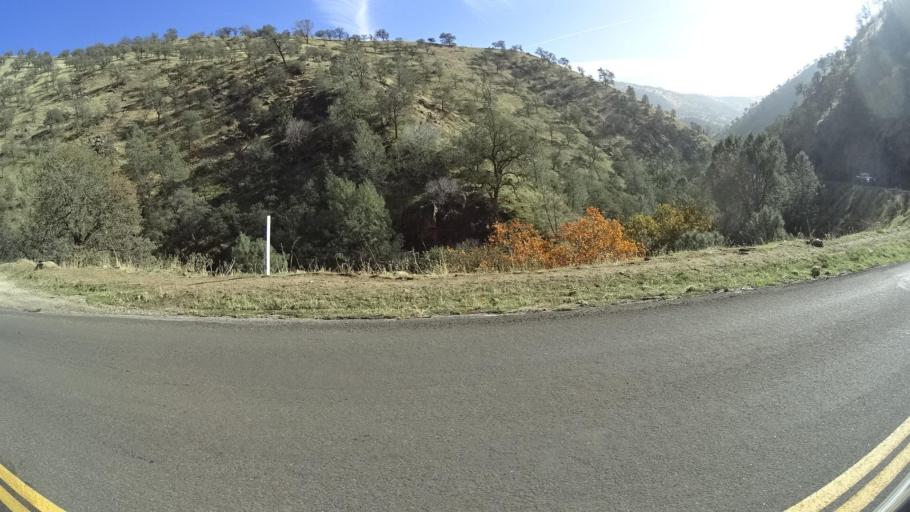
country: US
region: California
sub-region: Kern County
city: Bear Valley Springs
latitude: 35.3141
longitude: -118.5856
